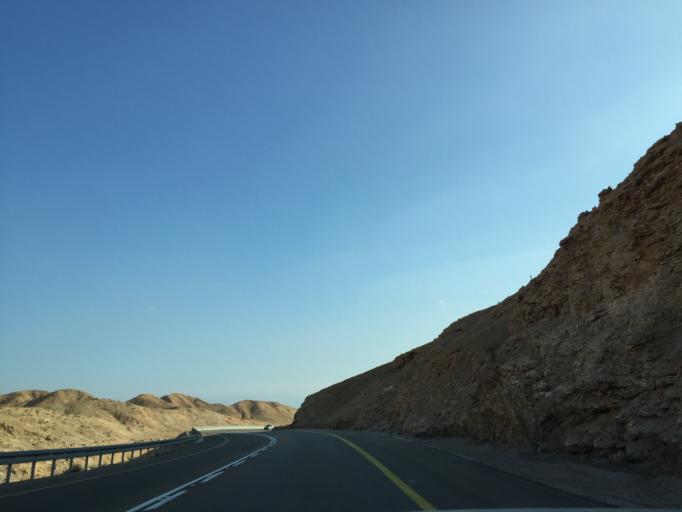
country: IL
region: Southern District
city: `En Boqeq
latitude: 31.1878
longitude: 35.2874
